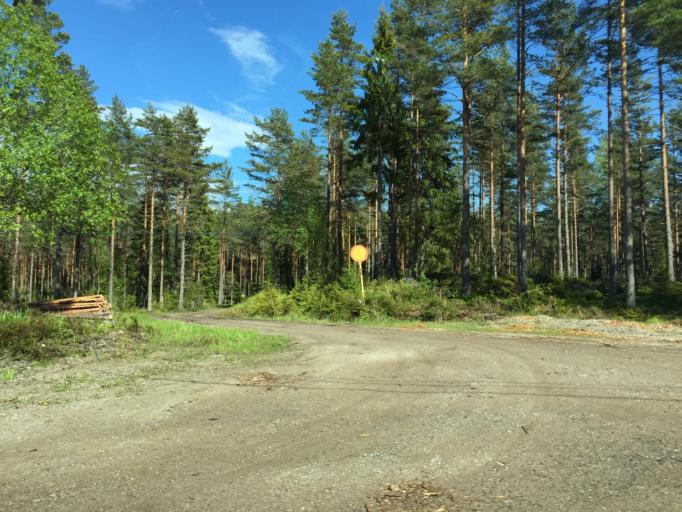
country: SE
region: Soedermanland
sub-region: Vingakers Kommun
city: Vingaker
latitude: 58.9755
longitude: 15.6815
